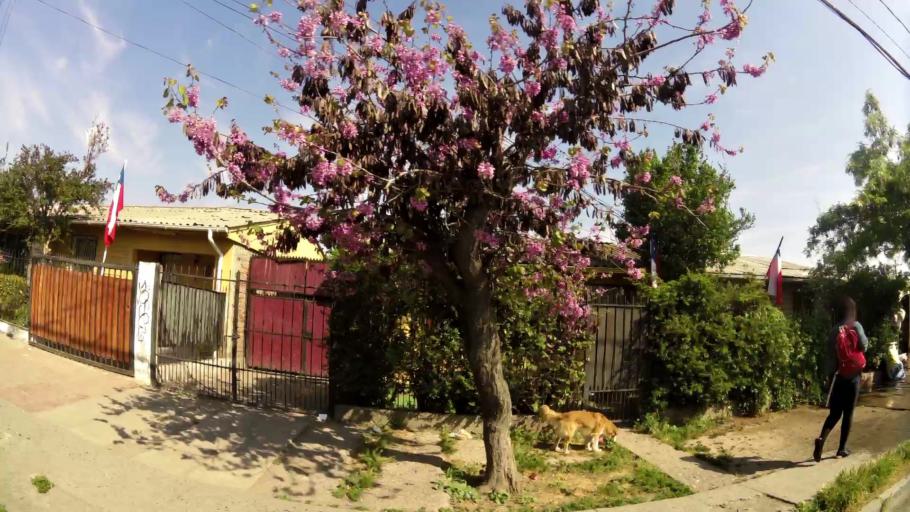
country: CL
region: Santiago Metropolitan
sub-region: Provincia de Santiago
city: La Pintana
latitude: -33.5593
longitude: -70.6641
